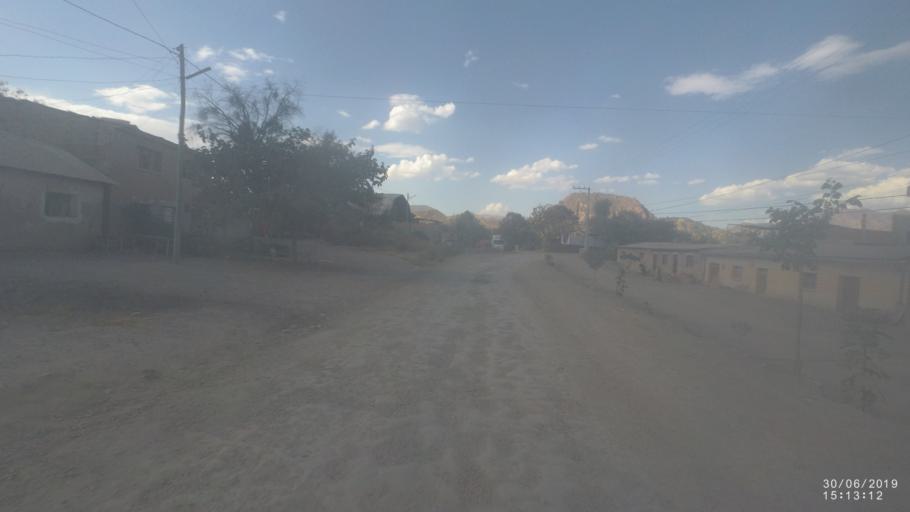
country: BO
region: Cochabamba
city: Irpa Irpa
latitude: -17.7233
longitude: -66.2835
